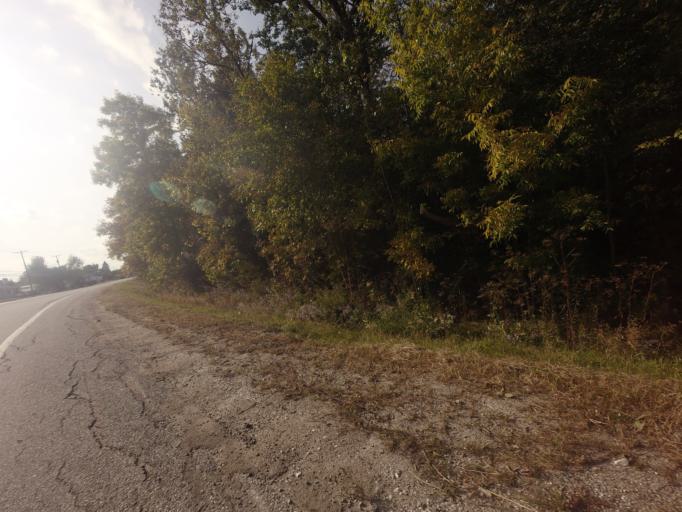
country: CA
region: Quebec
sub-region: Outaouais
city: Maniwaki
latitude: 46.3850
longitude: -75.9508
